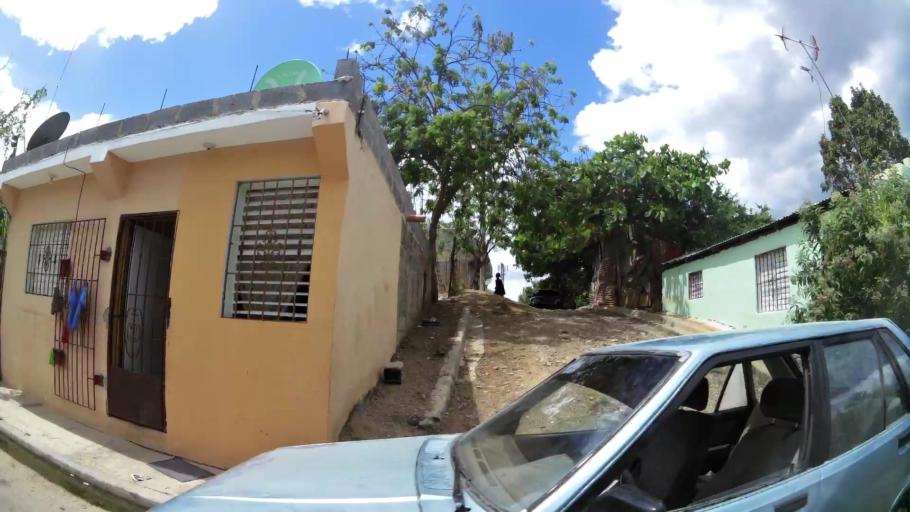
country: DO
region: Nacional
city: Ensanche Luperon
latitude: 18.5139
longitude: -69.9028
